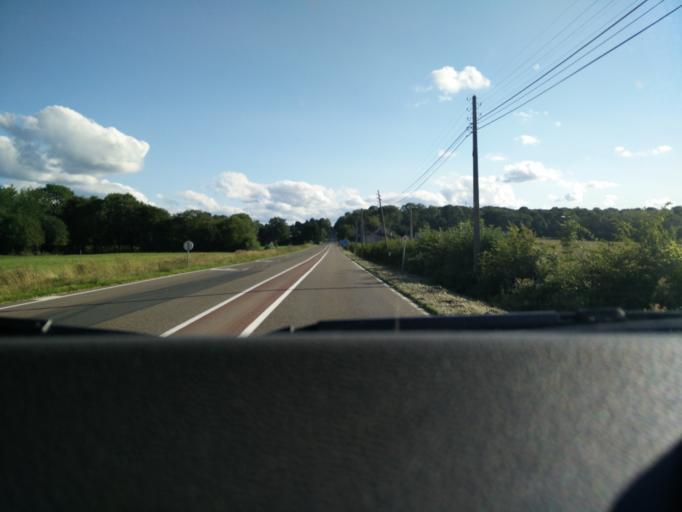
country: BE
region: Wallonia
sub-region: Province du Hainaut
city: Beaumont
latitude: 50.1944
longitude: 4.2219
